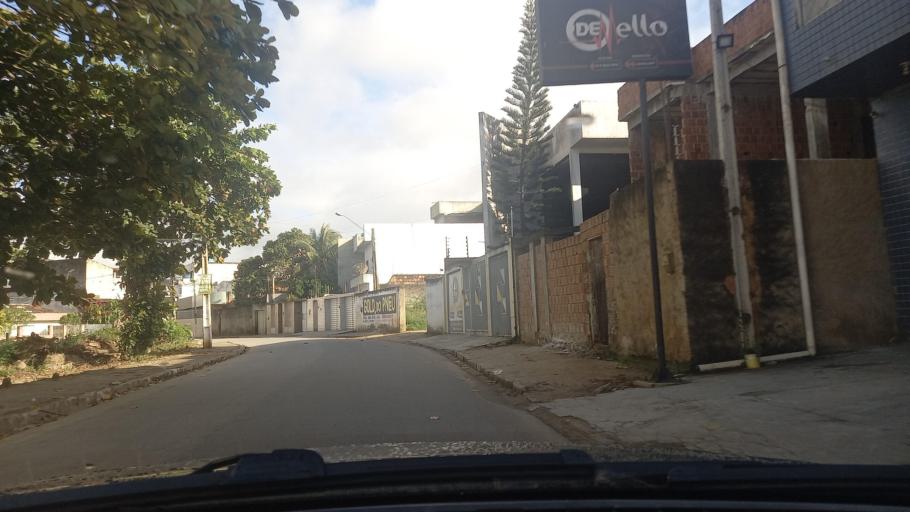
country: BR
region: Pernambuco
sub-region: Vitoria De Santo Antao
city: Vitoria de Santo Antao
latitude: -8.1071
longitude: -35.3015
